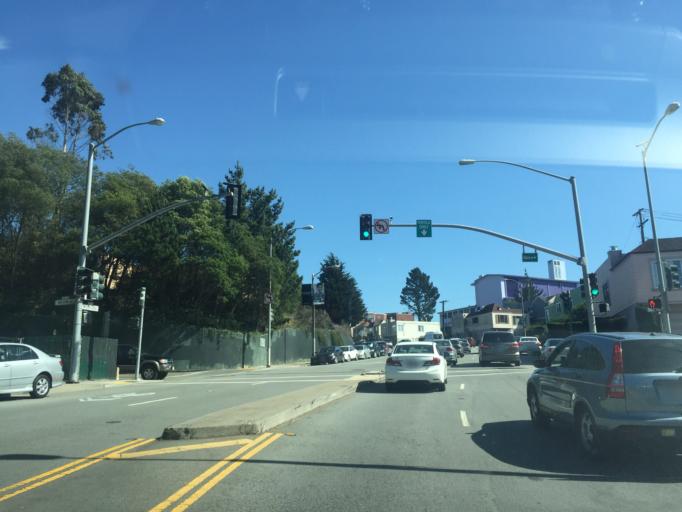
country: US
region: California
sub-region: San Mateo County
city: Daly City
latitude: 37.7461
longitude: -122.4548
